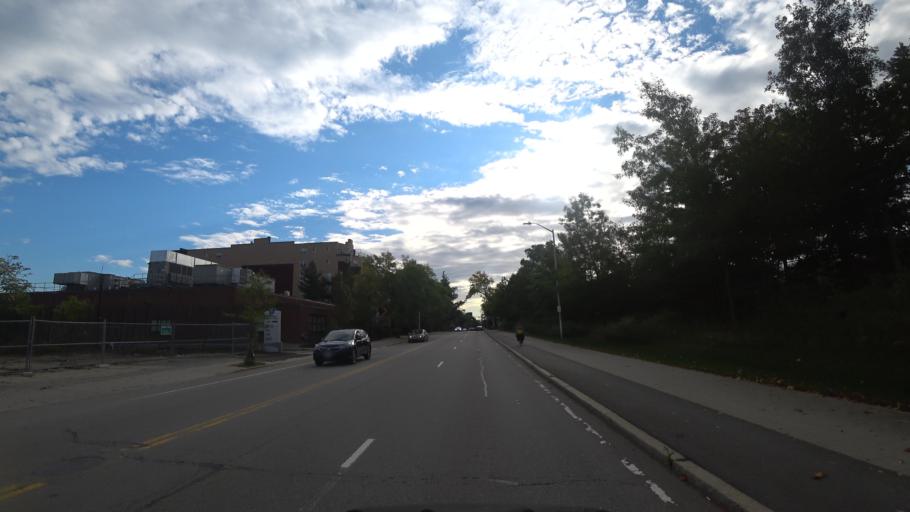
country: US
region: Massachusetts
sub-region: Middlesex County
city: Arlington
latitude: 42.3900
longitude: -71.1506
